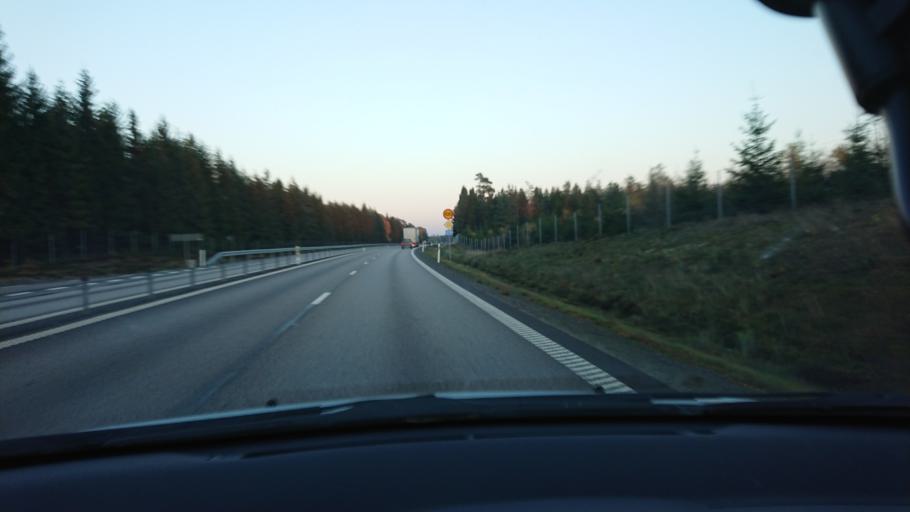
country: SE
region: Halland
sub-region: Laholms Kommun
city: Knared
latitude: 56.7207
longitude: 13.3262
